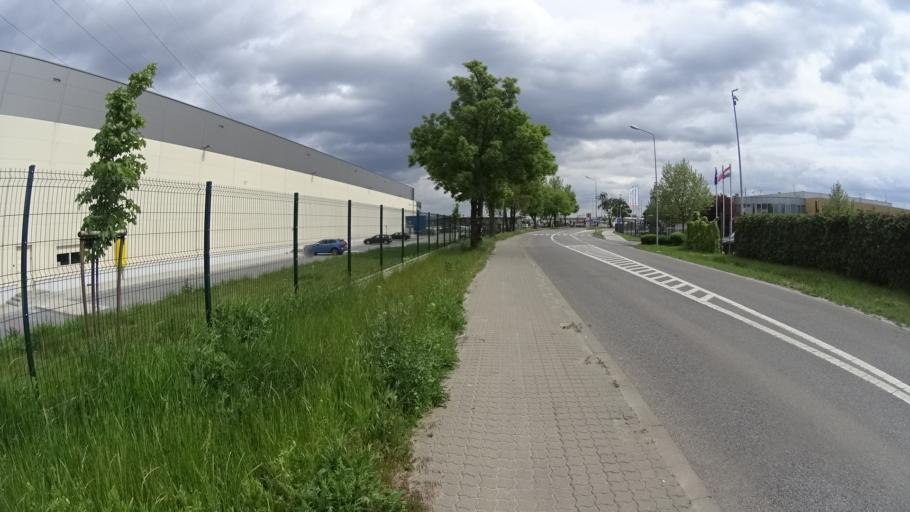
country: PL
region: Masovian Voivodeship
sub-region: Powiat warszawski zachodni
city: Babice
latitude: 52.2208
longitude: 20.8371
